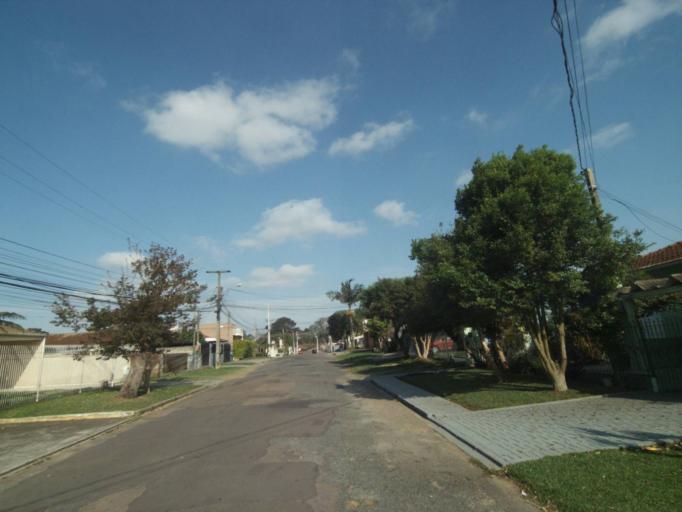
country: BR
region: Parana
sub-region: Curitiba
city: Curitiba
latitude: -25.4858
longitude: -49.3244
